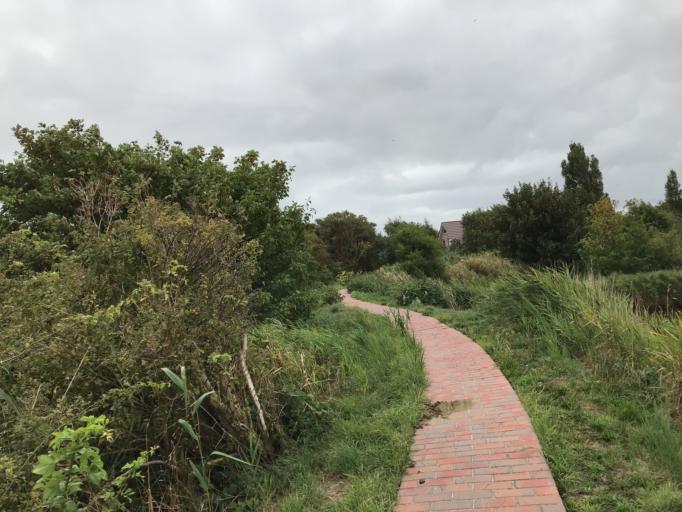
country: DE
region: Lower Saxony
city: Borkum
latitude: 53.5860
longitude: 6.6847
